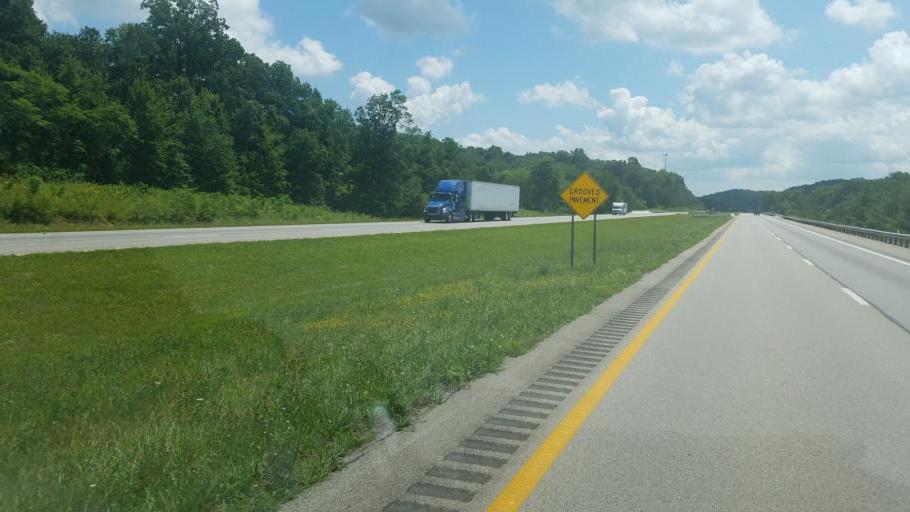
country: US
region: Ohio
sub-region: Jackson County
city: Jackson
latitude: 39.0840
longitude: -82.6410
